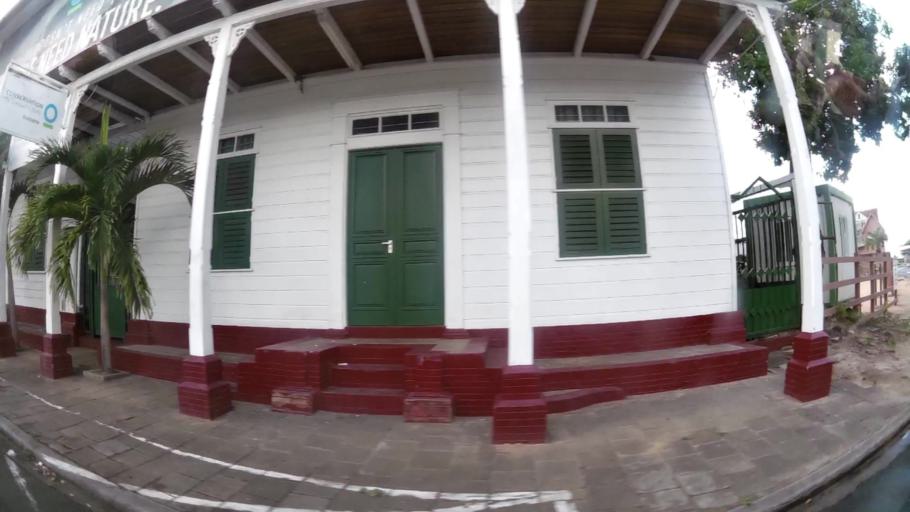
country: SR
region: Paramaribo
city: Paramaribo
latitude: 5.8264
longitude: -55.1540
